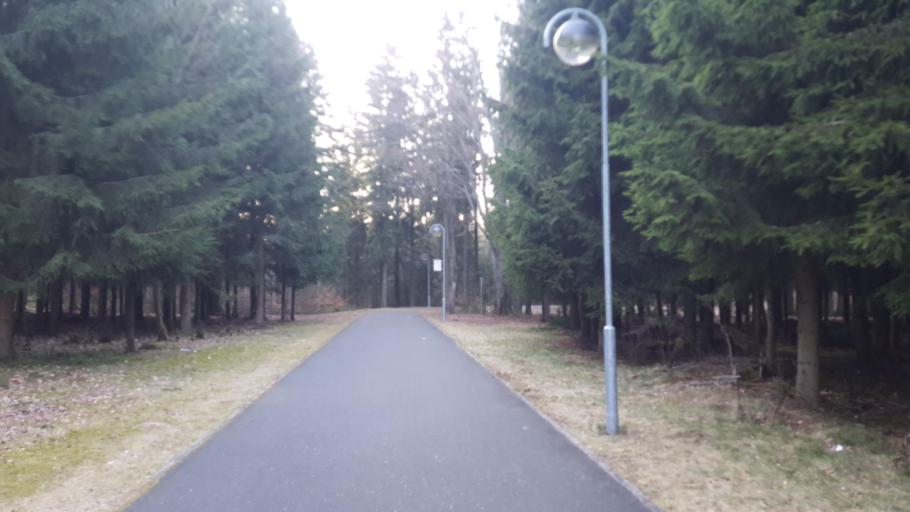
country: CZ
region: Karlovarsky
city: As
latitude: 50.2288
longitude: 12.2017
